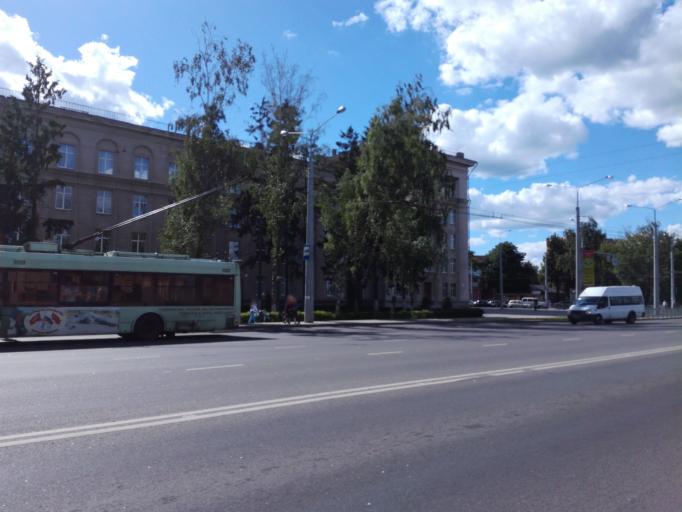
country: RU
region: Kursk
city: Kursk
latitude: 51.7652
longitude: 36.1837
